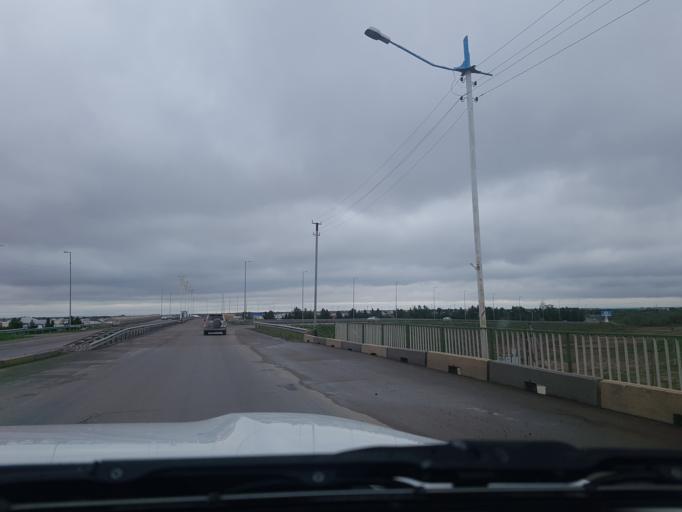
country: TM
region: Mary
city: Mary
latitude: 37.5972
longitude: 61.8872
